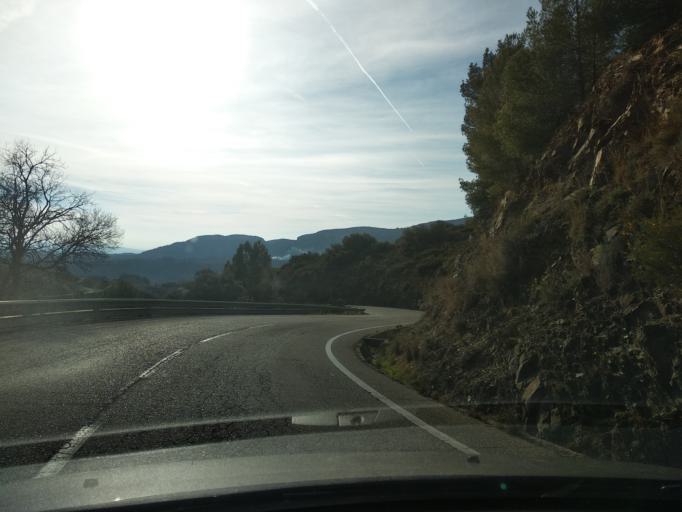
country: ES
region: Catalonia
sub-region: Provincia de Tarragona
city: Falset
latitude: 41.2093
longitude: 0.7747
